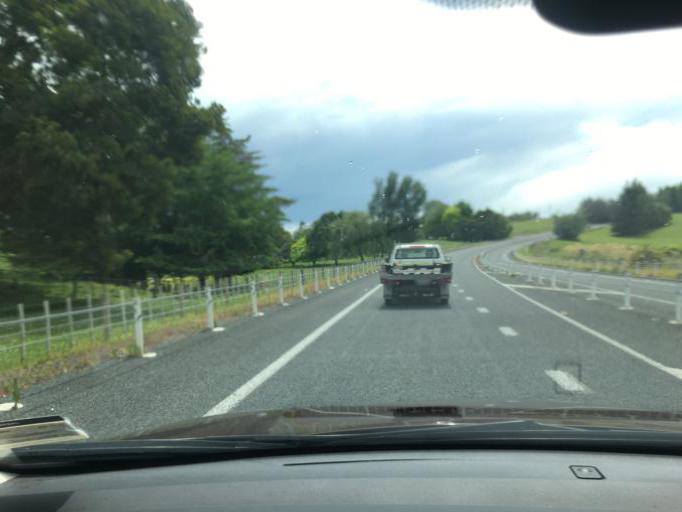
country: NZ
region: Waikato
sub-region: Waipa District
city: Cambridge
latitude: -37.9520
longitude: 175.3152
